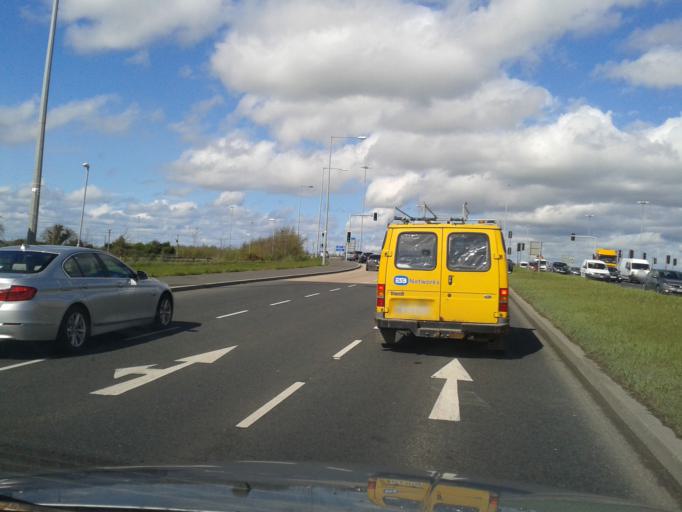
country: IE
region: Leinster
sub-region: Fingal County
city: Swords
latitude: 53.4762
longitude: -6.2071
